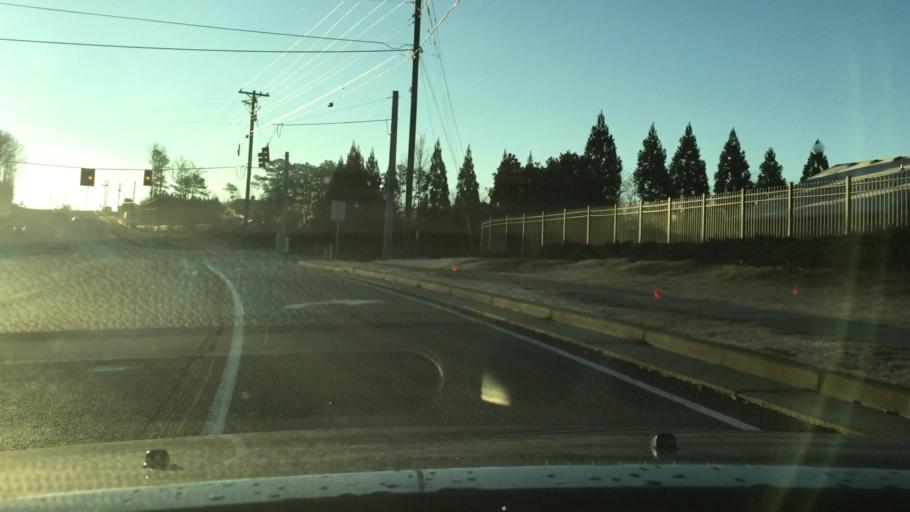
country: US
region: Georgia
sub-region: Forsyth County
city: Cumming
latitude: 34.1769
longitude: -84.1923
